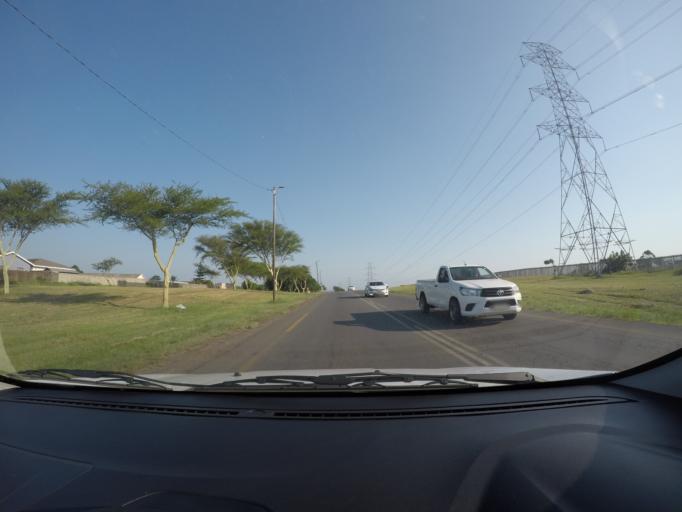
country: ZA
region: KwaZulu-Natal
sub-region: uThungulu District Municipality
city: Richards Bay
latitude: -28.7269
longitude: 32.0362
